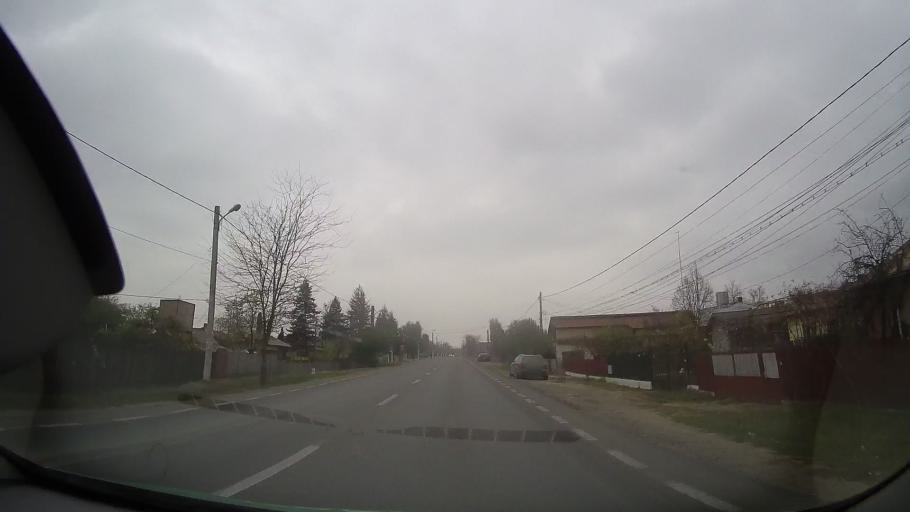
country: RO
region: Ialomita
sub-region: Comuna Manasia
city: Manasia
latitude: 44.7103
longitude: 26.6637
